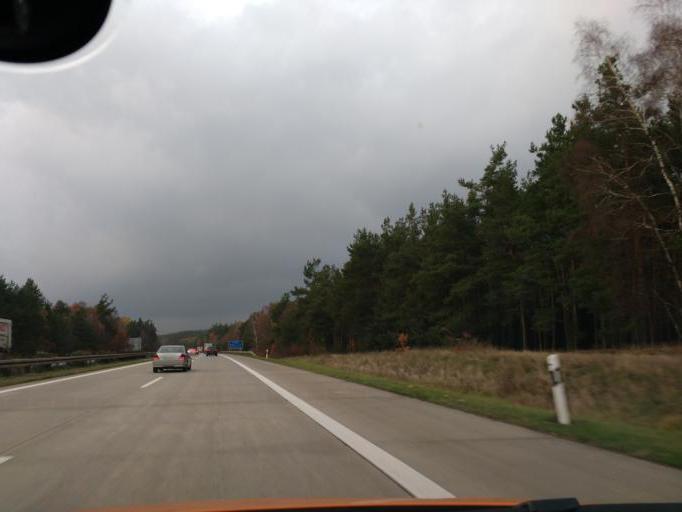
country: DE
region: Brandenburg
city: Heiligengrabe
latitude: 53.1552
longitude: 12.3982
